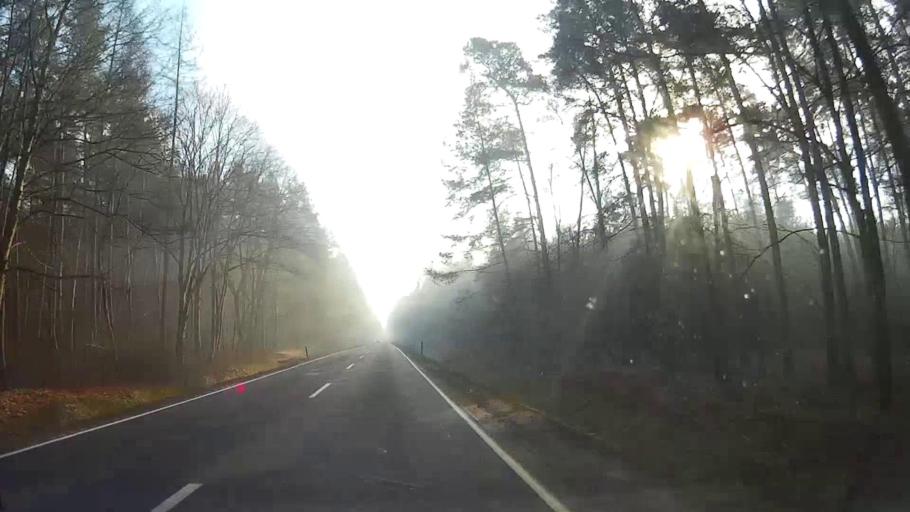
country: PL
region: Lesser Poland Voivodeship
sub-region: Powiat chrzanowski
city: Metkow
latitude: 50.0771
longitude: 19.3822
